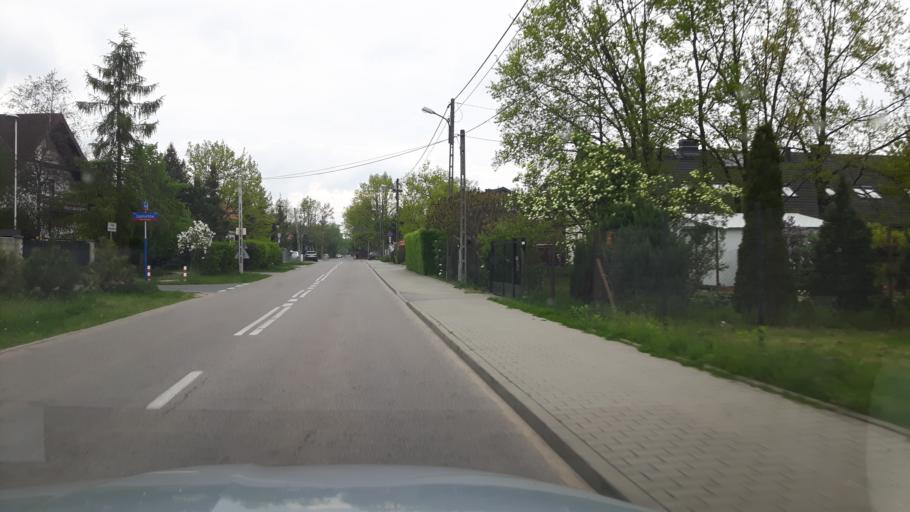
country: PL
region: Masovian Voivodeship
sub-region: Warszawa
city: Rembertow
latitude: 52.2704
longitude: 21.1607
